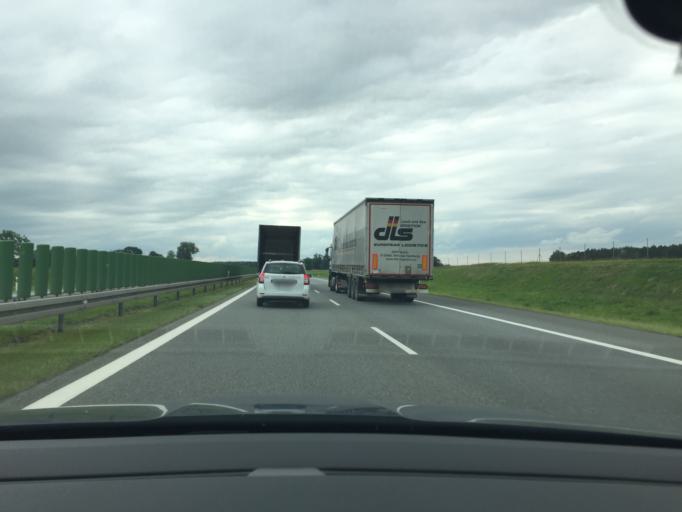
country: PL
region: Greater Poland Voivodeship
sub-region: Powiat poznanski
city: Buk
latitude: 52.3853
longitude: 16.5356
